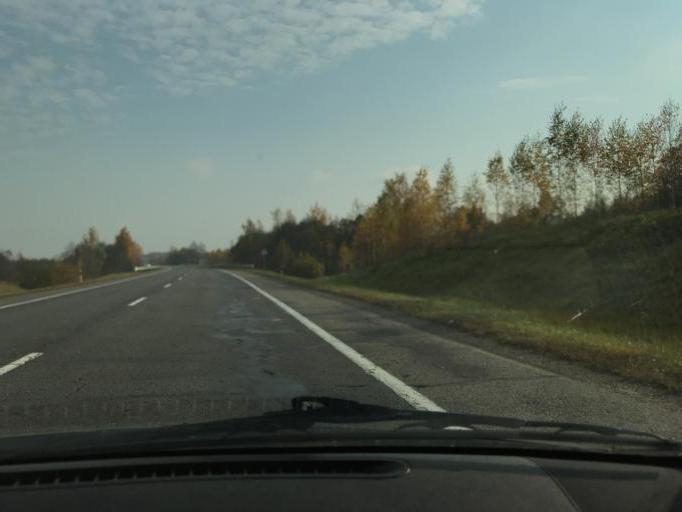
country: BY
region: Vitebsk
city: Lyepyel'
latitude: 54.9890
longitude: 28.8886
